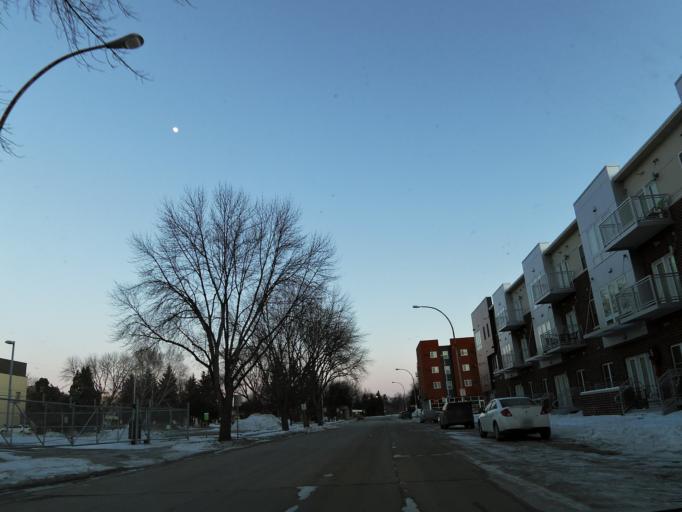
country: US
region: North Dakota
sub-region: Grand Forks County
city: Grand Forks
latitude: 47.9241
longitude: -97.0356
